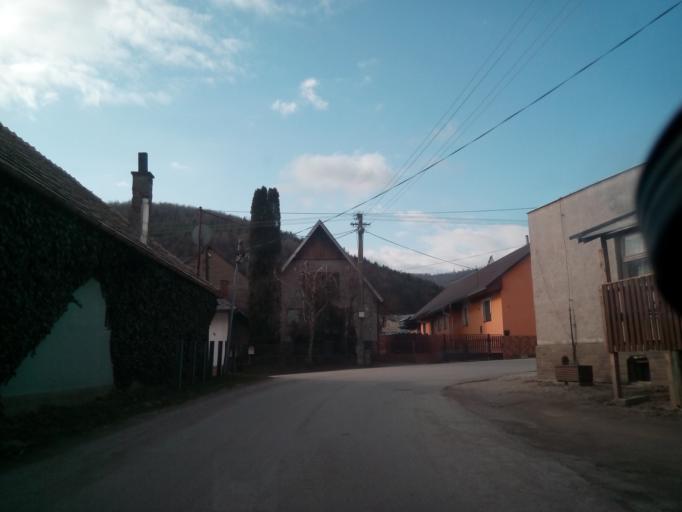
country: SK
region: Banskobystricky
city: Revuca
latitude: 48.7226
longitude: 20.2547
